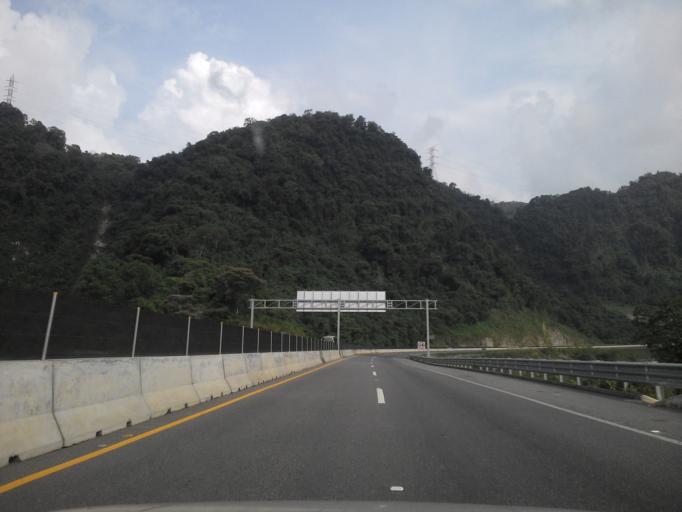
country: MX
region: Puebla
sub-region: Xicotepec
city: San Lorenzo
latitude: 20.3386
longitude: -97.9597
